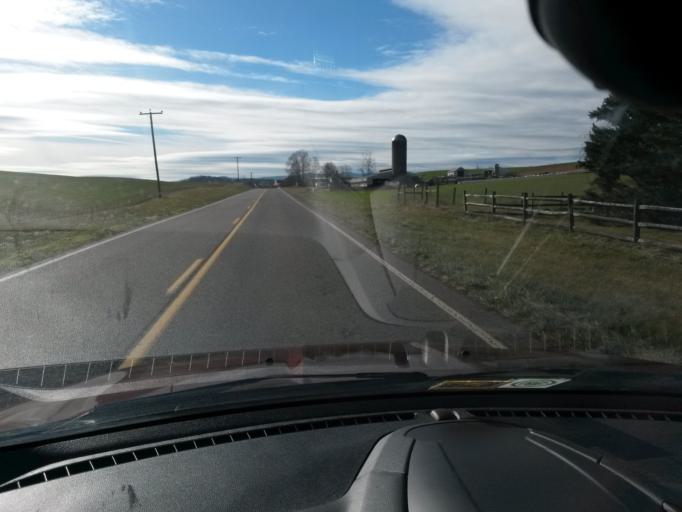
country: US
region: Virginia
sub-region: Rockingham County
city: Bridgewater
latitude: 38.3138
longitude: -79.0969
